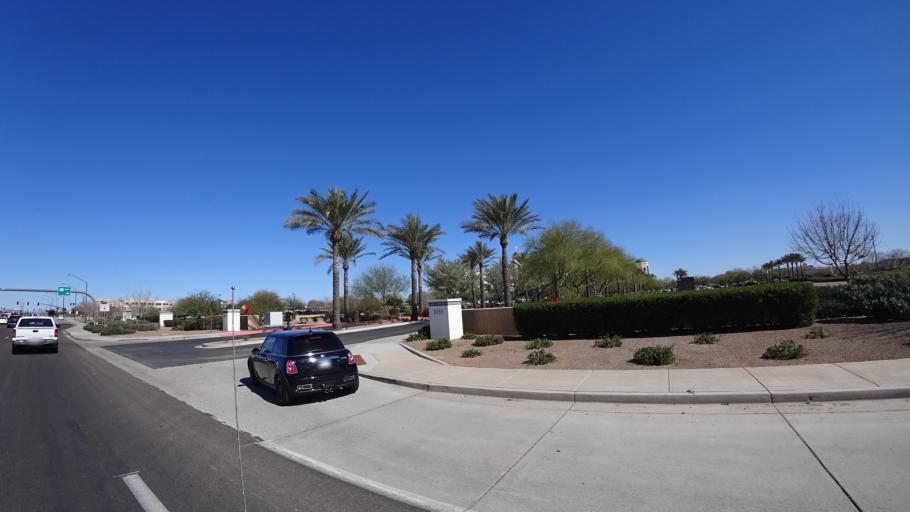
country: US
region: Arizona
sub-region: Maricopa County
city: Gilbert
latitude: 33.2858
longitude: -111.7553
